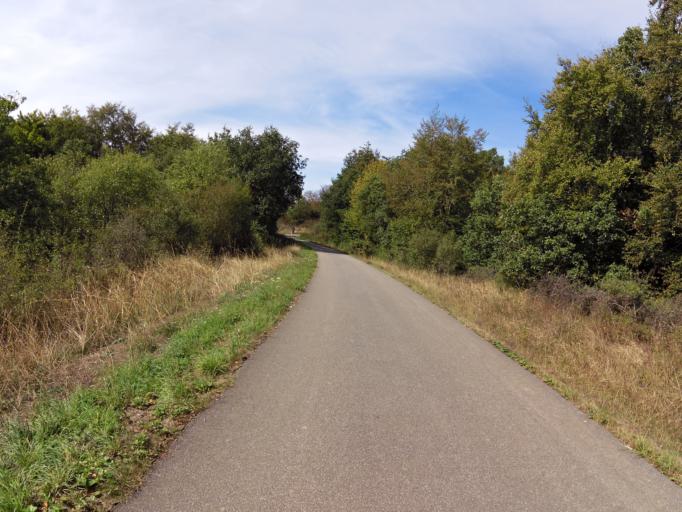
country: DE
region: Rheinland-Pfalz
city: Lichtenborn
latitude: 50.1148
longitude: 6.2784
